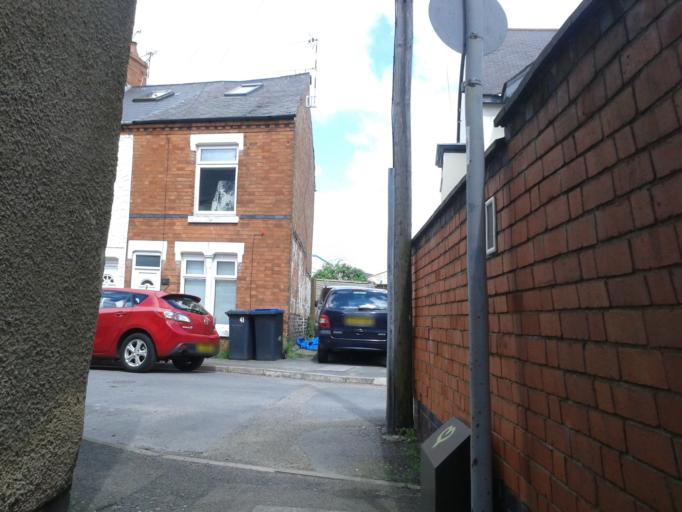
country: GB
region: England
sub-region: Leicestershire
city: Hinckley
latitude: 52.5446
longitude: -1.3661
